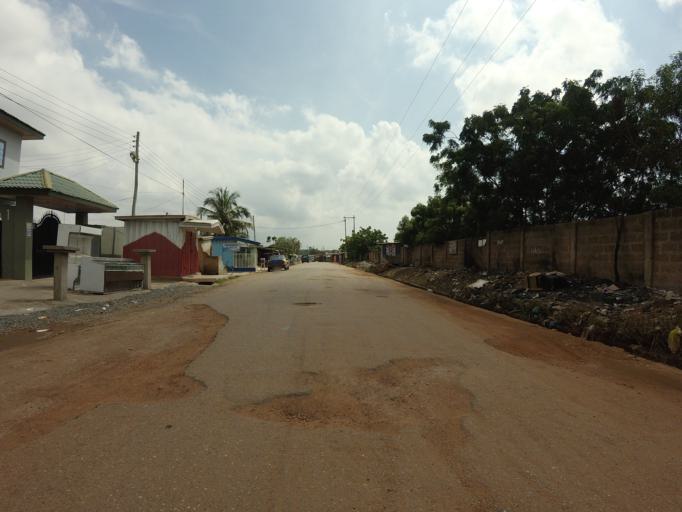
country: GH
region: Greater Accra
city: Nungua
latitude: 5.6087
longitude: -0.0845
